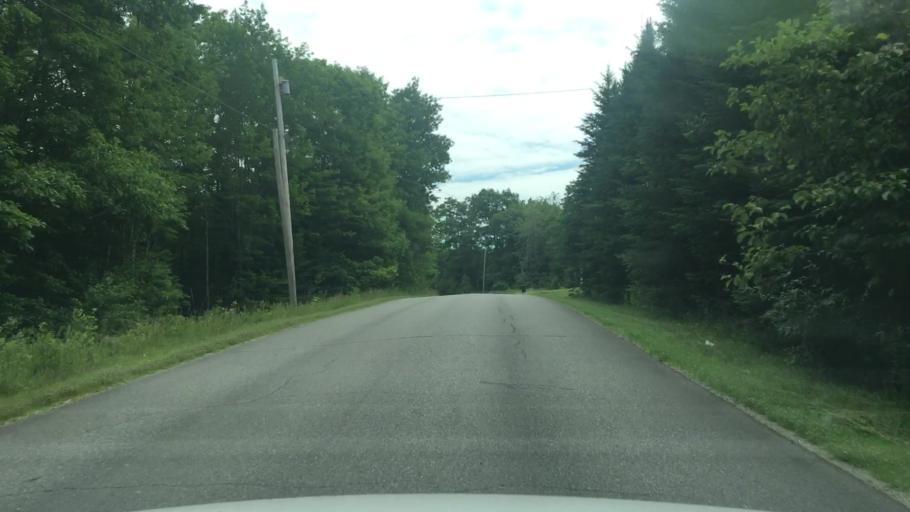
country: US
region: Maine
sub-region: Kennebec County
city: Albion
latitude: 44.4746
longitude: -69.3604
